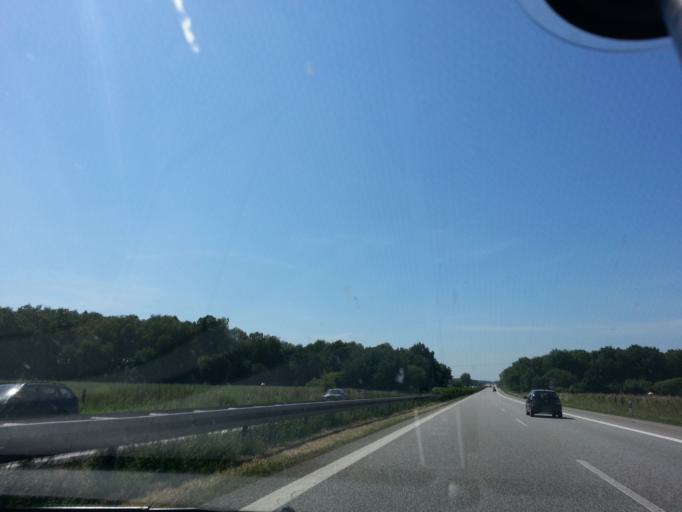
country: DE
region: Mecklenburg-Vorpommern
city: Wittenburg
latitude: 53.4993
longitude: 11.0678
